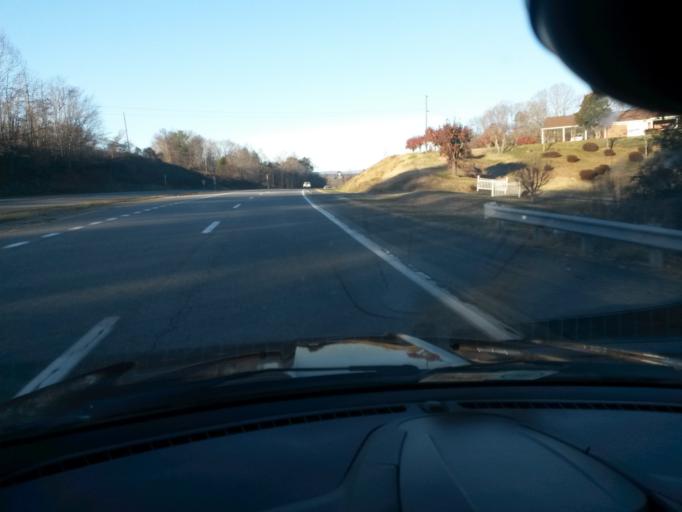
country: US
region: Virginia
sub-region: Henry County
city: Horse Pasture
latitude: 36.6218
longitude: -79.9823
